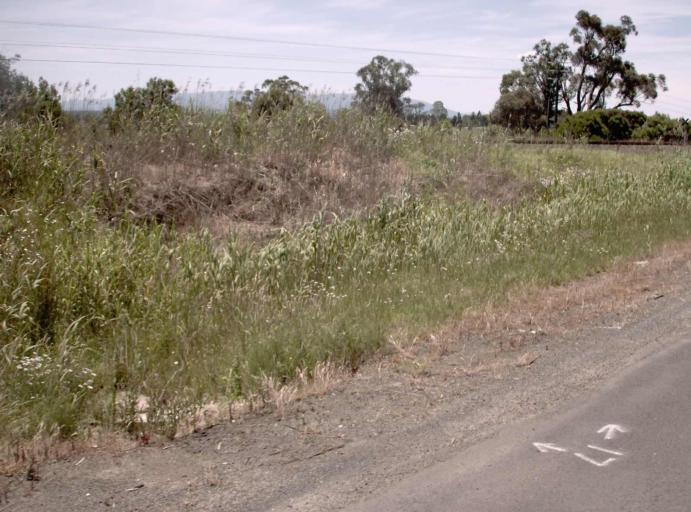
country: AU
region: Victoria
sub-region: Latrobe
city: Moe
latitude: -38.2007
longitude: 146.1922
